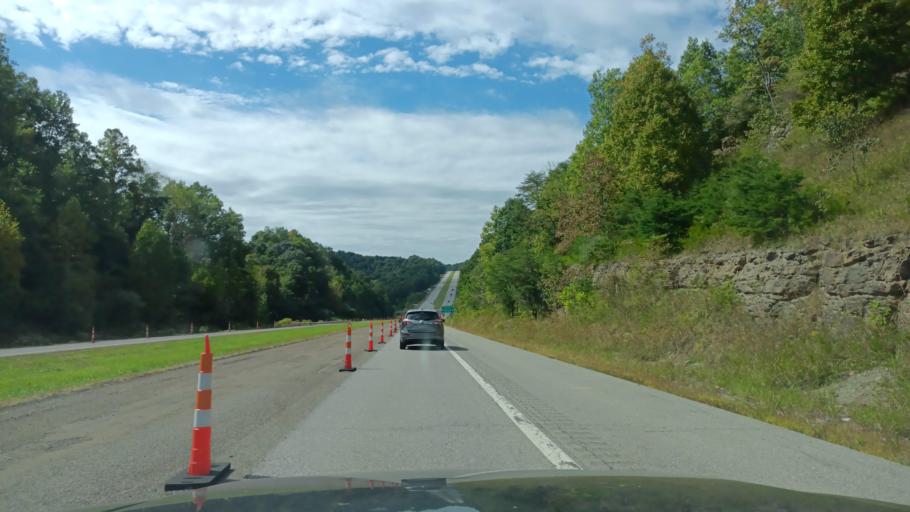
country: US
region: West Virginia
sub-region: Ritchie County
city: Harrisville
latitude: 39.2613
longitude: -81.1339
